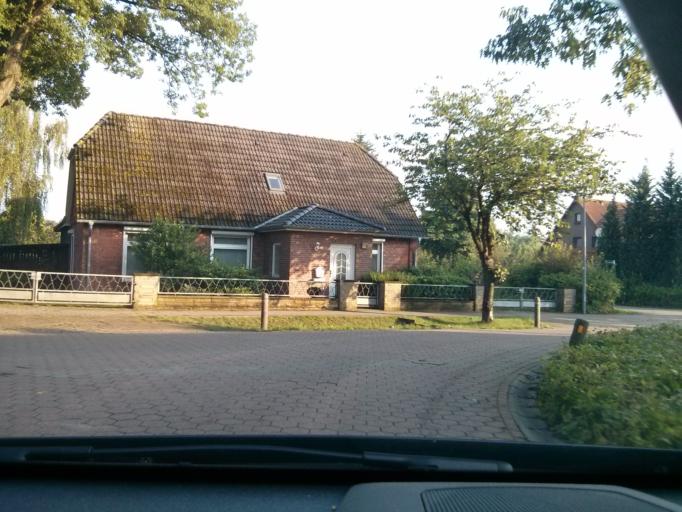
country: DE
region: Lower Saxony
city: Jesteburg
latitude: 53.3002
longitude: 9.9512
